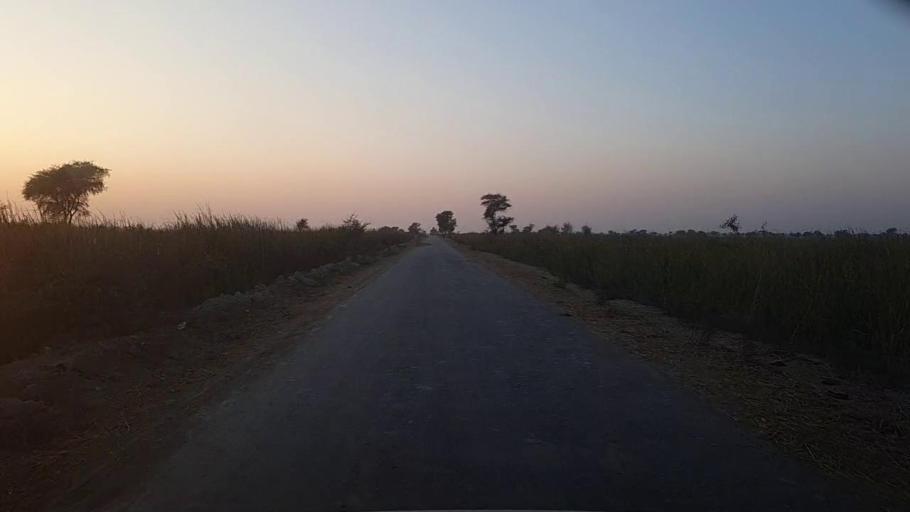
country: PK
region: Sindh
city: Khairpur Nathan Shah
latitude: 27.1593
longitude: 67.7099
